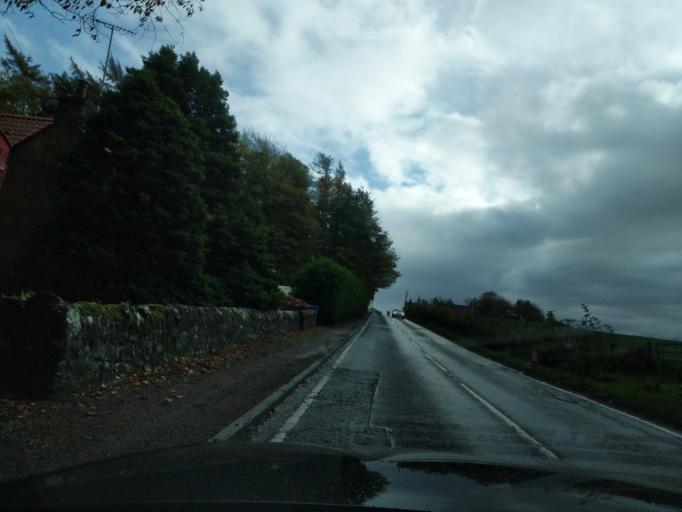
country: GB
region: Scotland
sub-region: Fife
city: Saint Andrews
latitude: 56.2907
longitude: -2.7494
